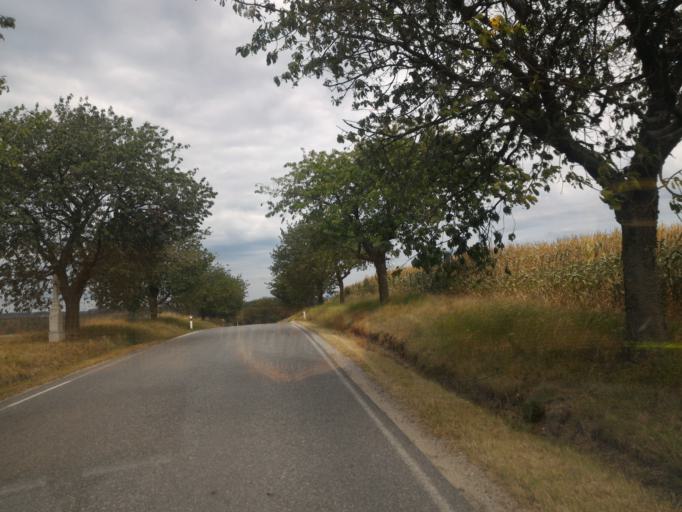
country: CZ
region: Jihocesky
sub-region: Okres Jindrichuv Hradec
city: Dacice
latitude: 49.1077
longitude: 15.4993
